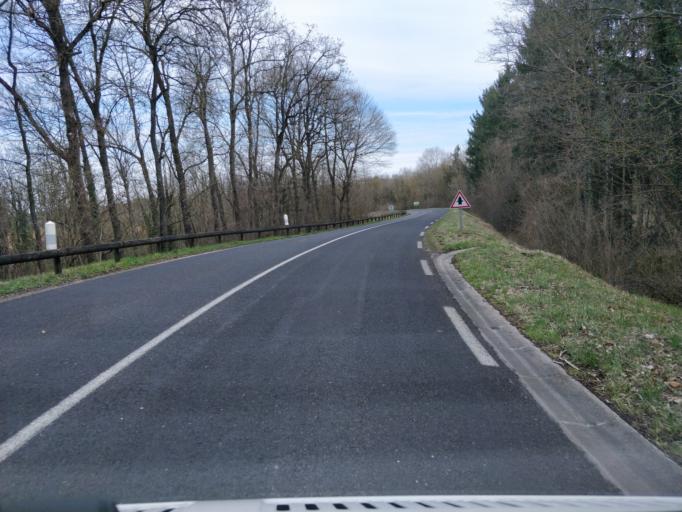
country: FR
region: Lorraine
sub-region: Departement de Meurthe-et-Moselle
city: Montauville
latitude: 48.9384
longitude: 5.8842
